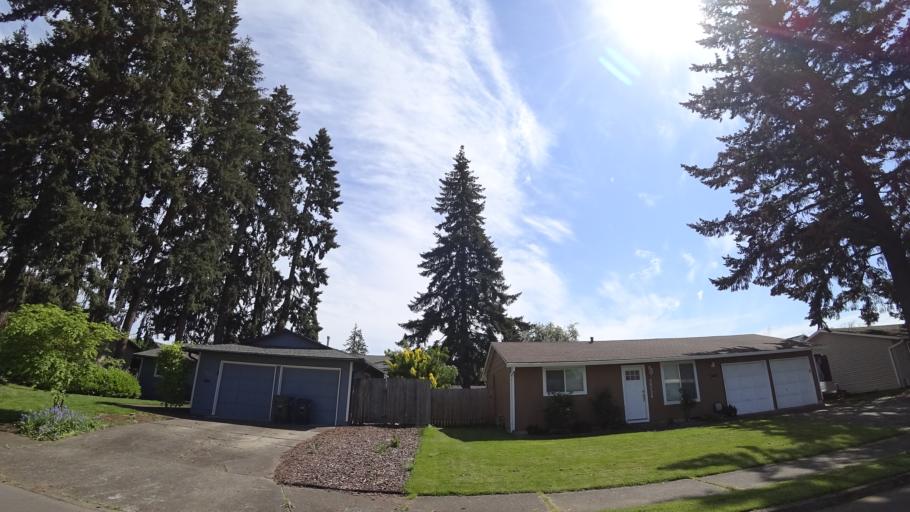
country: US
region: Oregon
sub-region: Washington County
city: Aloha
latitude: 45.4910
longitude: -122.8901
